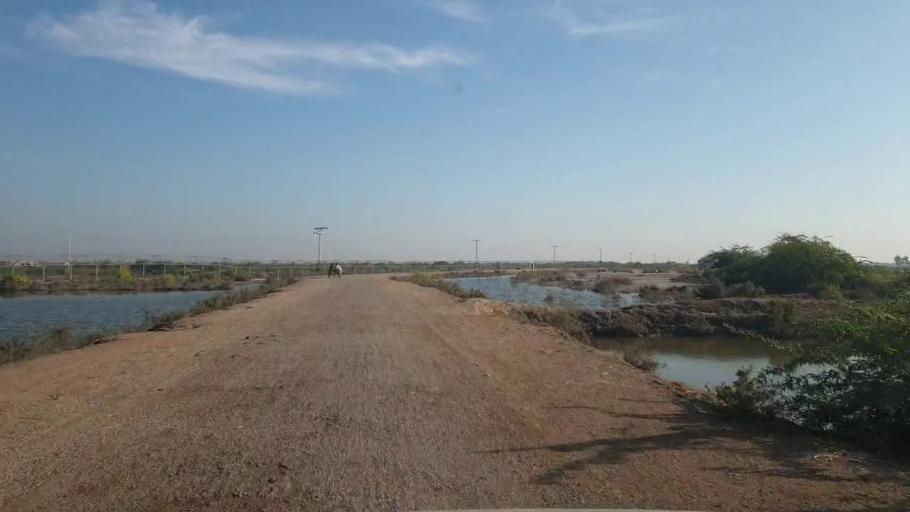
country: PK
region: Sindh
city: Talhar
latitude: 24.8386
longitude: 68.8470
